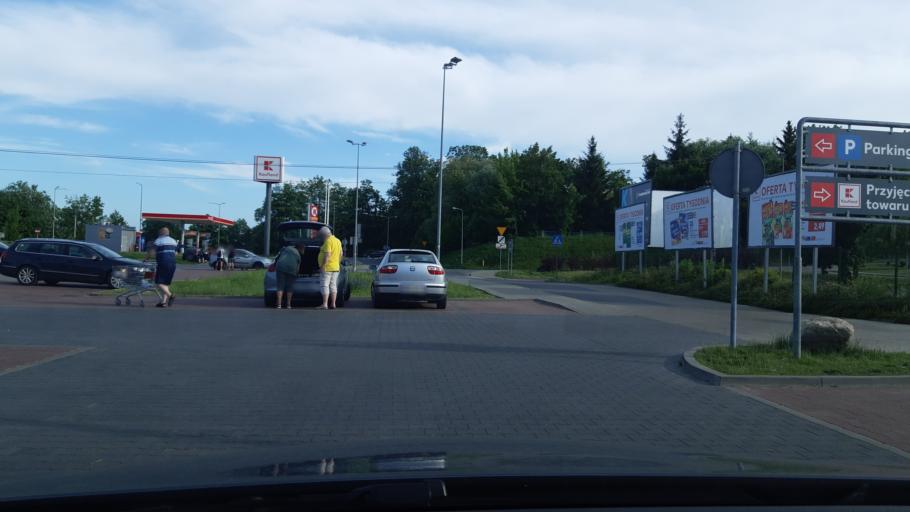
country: PL
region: Warmian-Masurian Voivodeship
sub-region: Powiat mragowski
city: Mragowo
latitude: 53.8785
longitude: 21.3064
